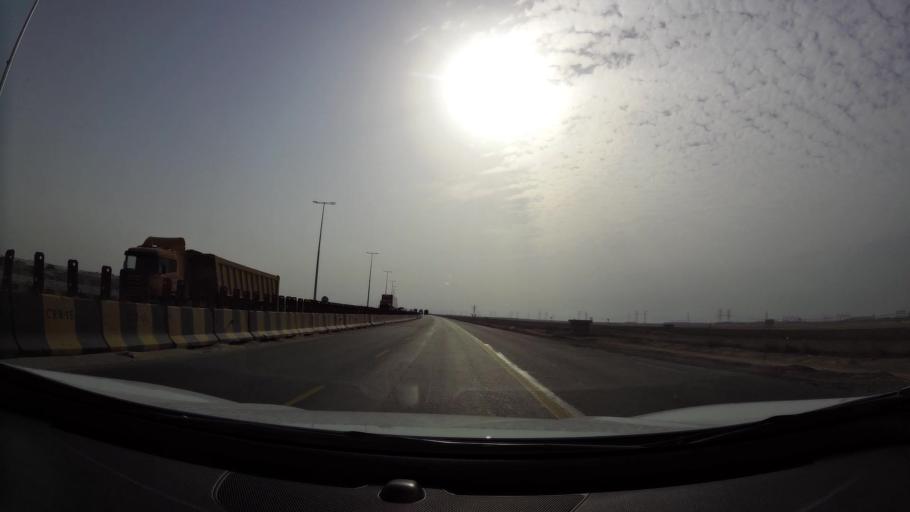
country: AE
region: Abu Dhabi
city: Abu Dhabi
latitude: 24.2685
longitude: 54.4973
